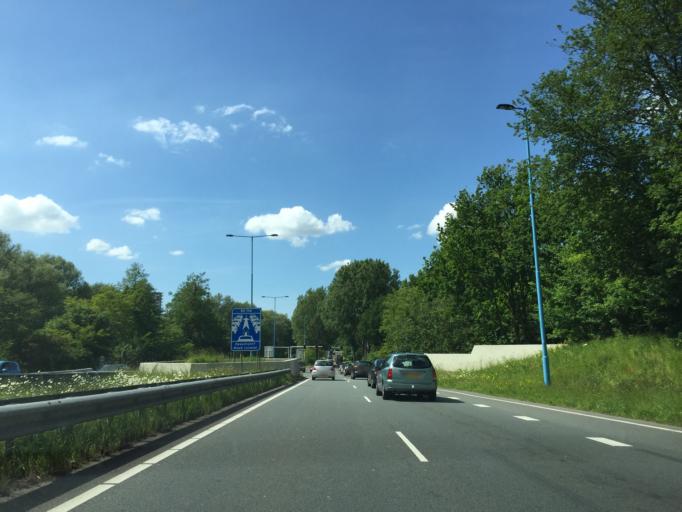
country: NL
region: South Holland
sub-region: Gemeente Zoetermeer
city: Zoetermeer
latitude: 52.0571
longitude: 4.5143
